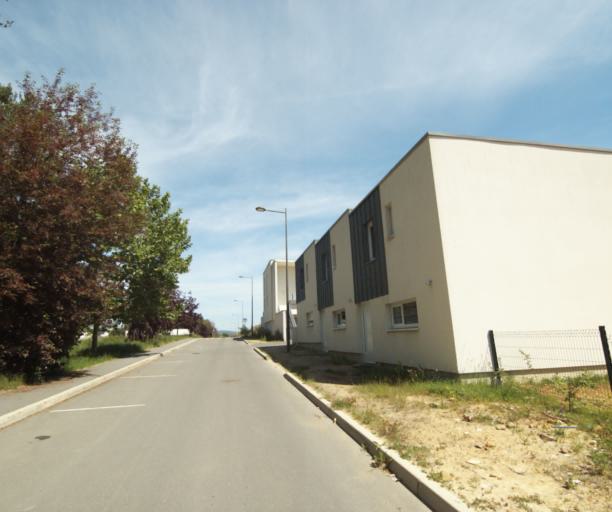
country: FR
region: Champagne-Ardenne
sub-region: Departement des Ardennes
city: Charleville-Mezieres
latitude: 49.7502
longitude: 4.7177
